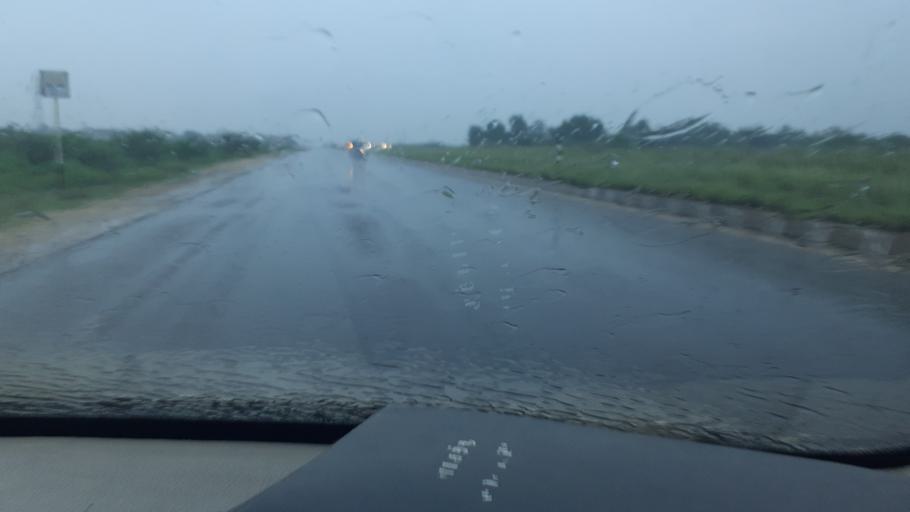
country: IN
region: Tamil Nadu
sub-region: Virudhunagar
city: Sattur
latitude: 9.4219
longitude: 77.9173
